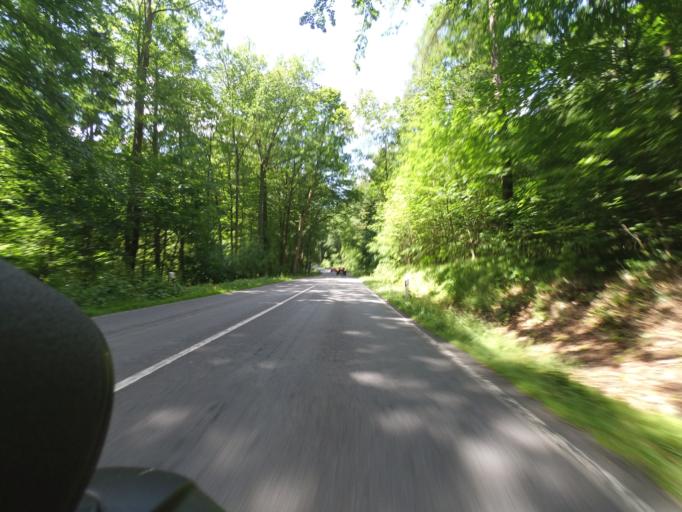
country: DE
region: Saxony
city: Stadt Wehlen
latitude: 50.9879
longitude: 14.0340
